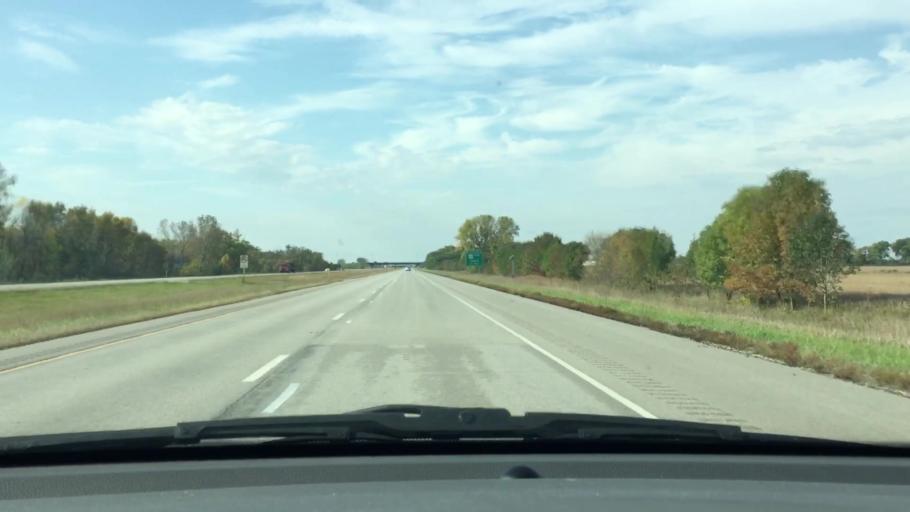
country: US
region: Illinois
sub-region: Rock Island County
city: Port Byron
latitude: 41.5655
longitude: -90.2306
